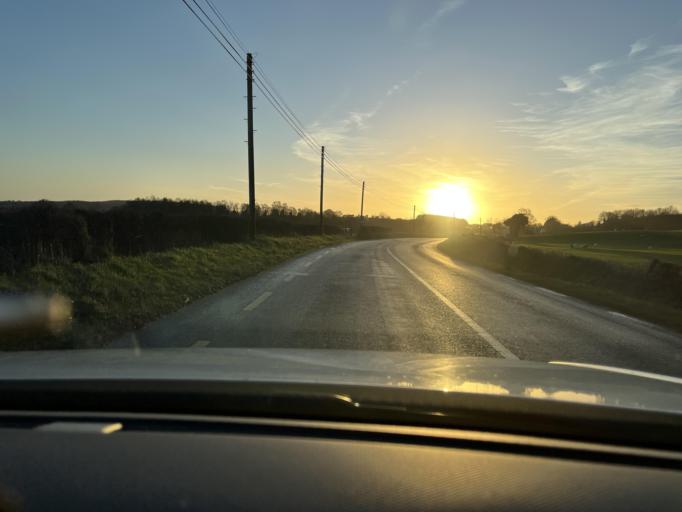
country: IE
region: Ulster
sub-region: An Cabhan
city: Ballyconnell
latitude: 54.1021
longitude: -7.6013
